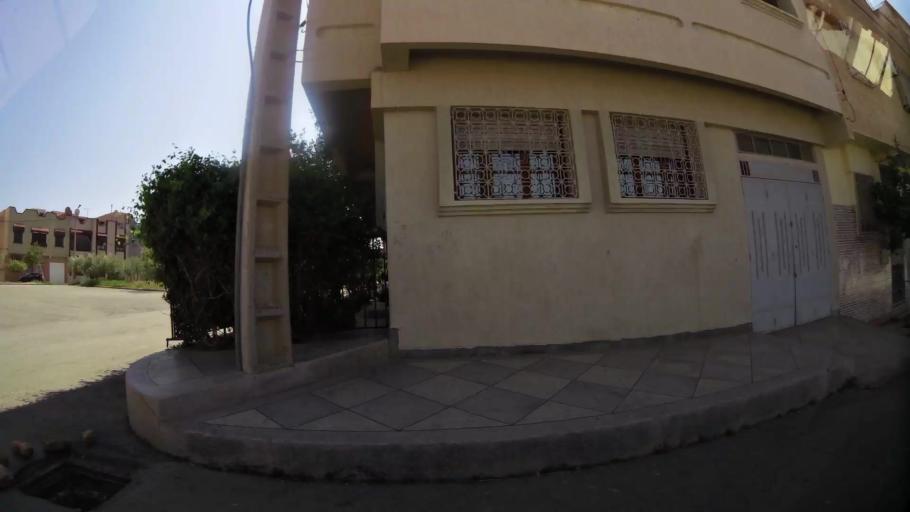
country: MA
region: Oriental
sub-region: Oujda-Angad
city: Oujda
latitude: 34.6928
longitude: -1.8758
